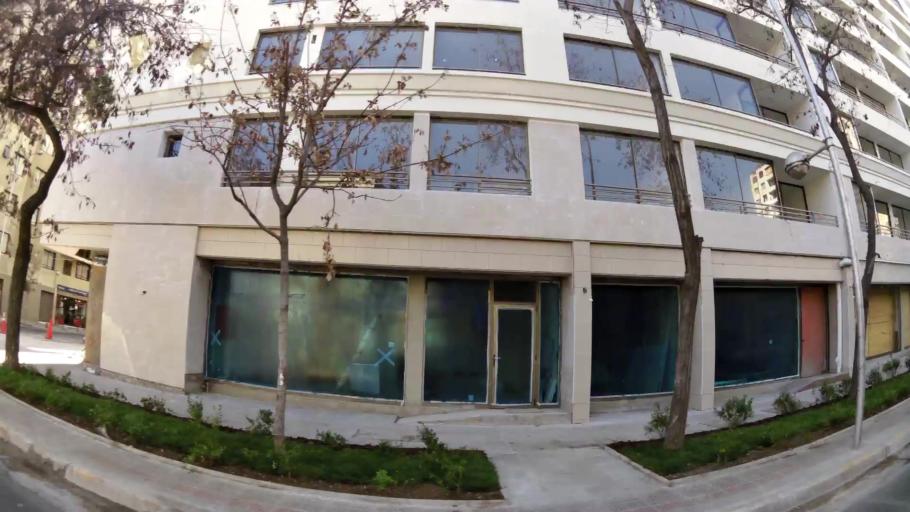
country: CL
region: Santiago Metropolitan
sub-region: Provincia de Santiago
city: Santiago
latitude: -33.4458
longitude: -70.6349
